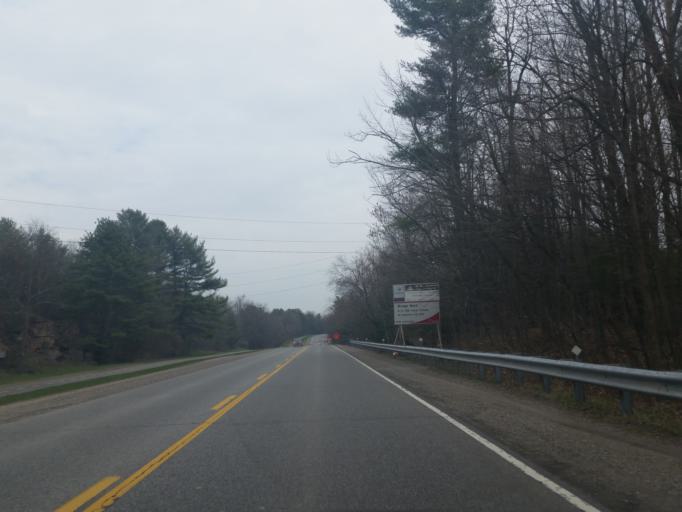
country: US
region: New York
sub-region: Jefferson County
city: Alexandria Bay
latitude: 44.3679
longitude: -75.9966
